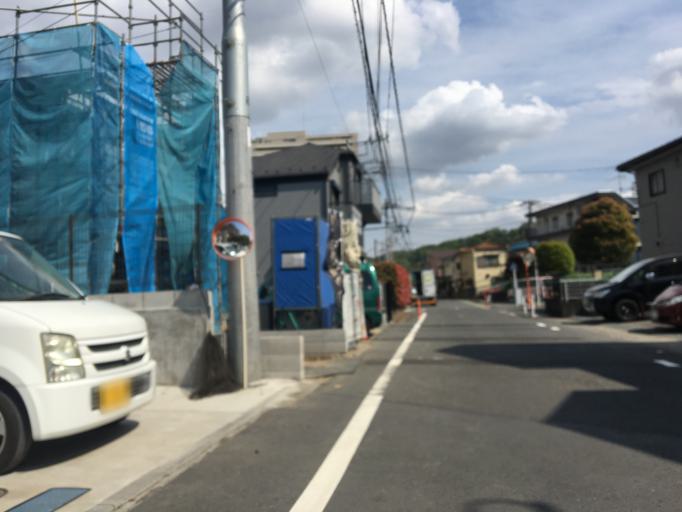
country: JP
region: Tokyo
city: Chofugaoka
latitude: 35.6355
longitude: 139.5132
